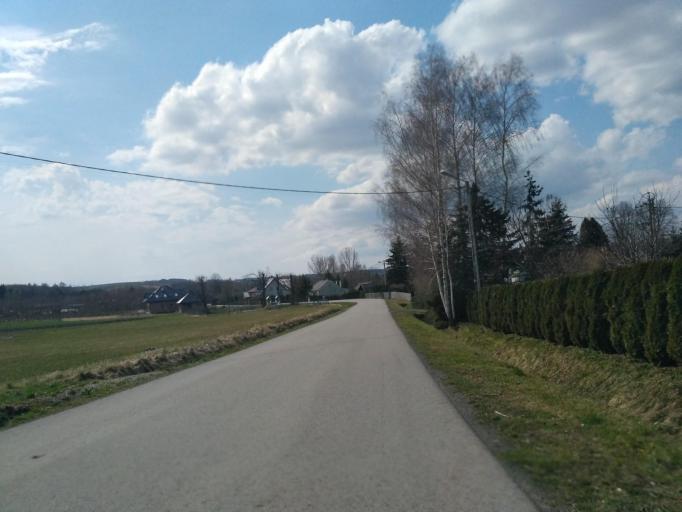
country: PL
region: Subcarpathian Voivodeship
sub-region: Powiat ropczycko-sedziszowski
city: Iwierzyce
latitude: 50.0056
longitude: 21.7640
